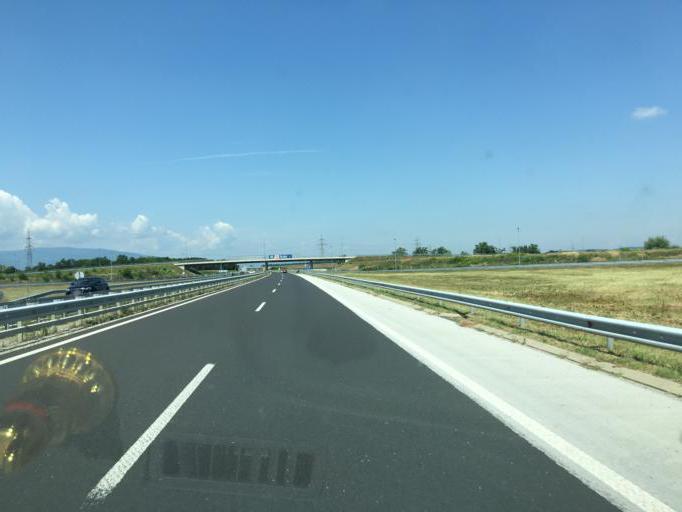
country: SI
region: Starse
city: Starse
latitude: 46.4405
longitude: 15.7827
